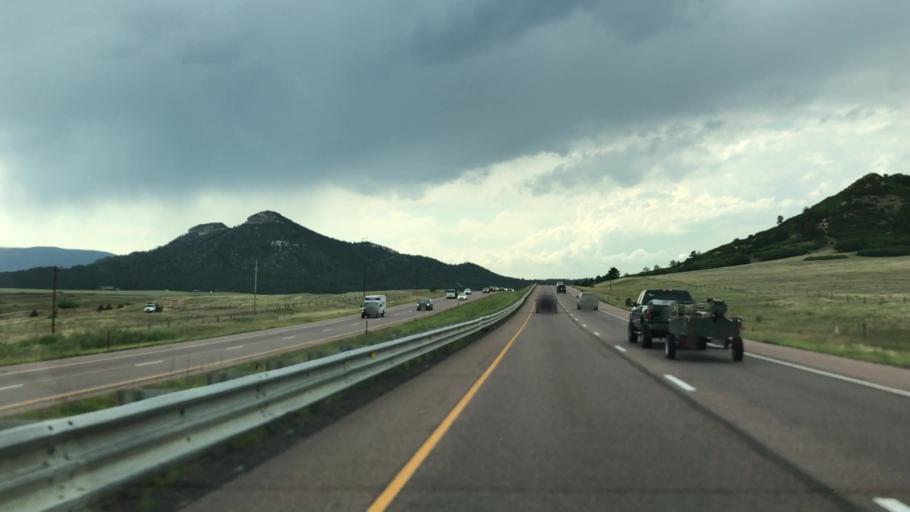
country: US
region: Colorado
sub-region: El Paso County
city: Palmer Lake
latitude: 39.2105
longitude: -104.8675
